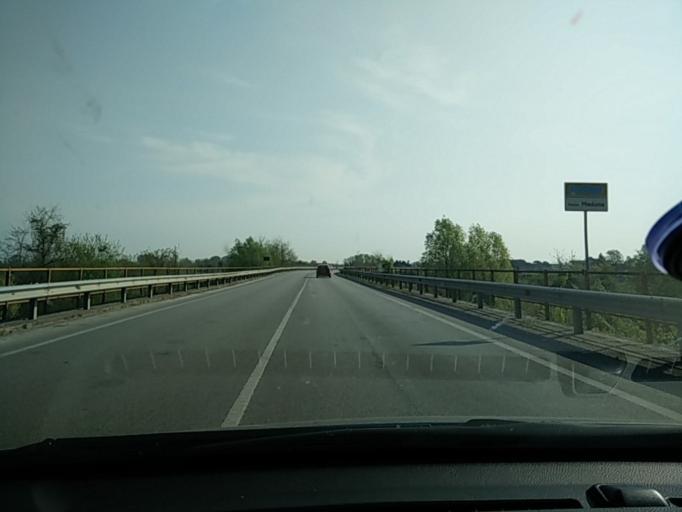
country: IT
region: Friuli Venezia Giulia
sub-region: Provincia di Pordenone
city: Prata di Sotto
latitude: 45.8983
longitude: 12.6031
